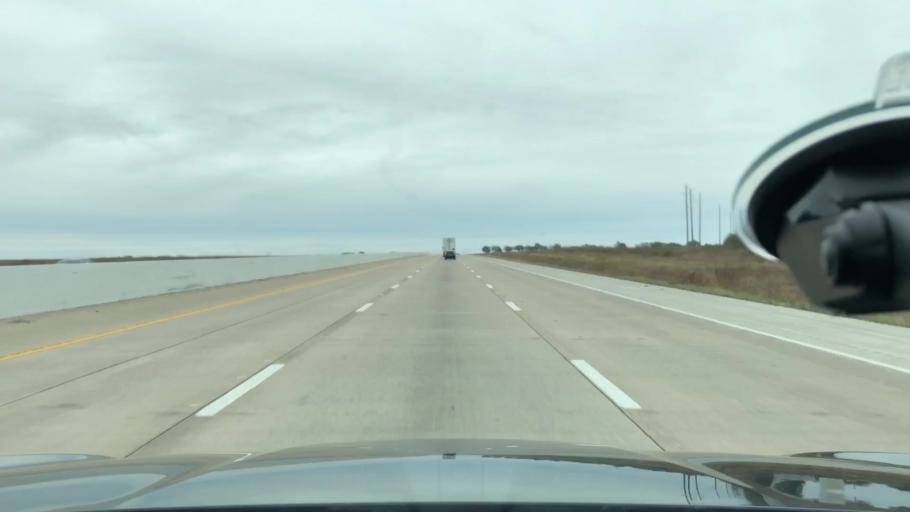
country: US
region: Texas
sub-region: Ellis County
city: Italy
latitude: 32.1592
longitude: -96.9241
